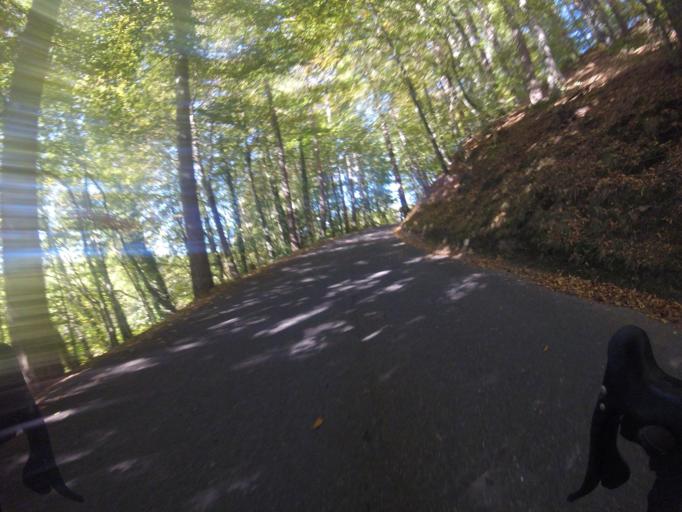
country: CH
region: Bern
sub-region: Bern-Mittelland District
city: Wohlen
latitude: 46.9693
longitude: 7.3517
